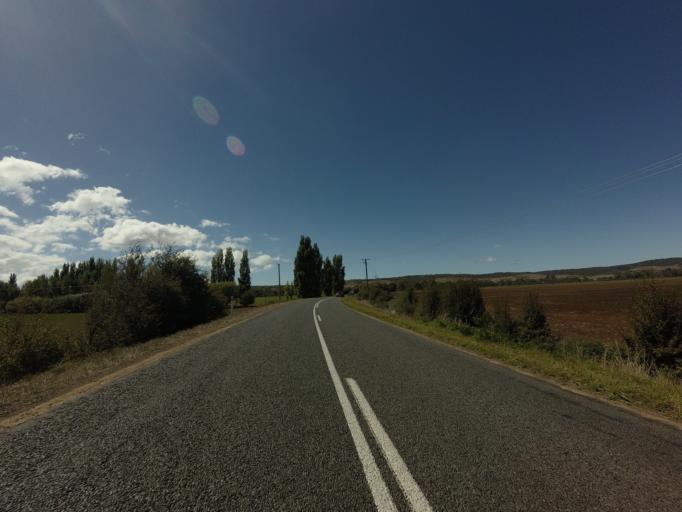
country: AU
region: Tasmania
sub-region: Break O'Day
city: St Helens
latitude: -41.9964
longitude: 148.0741
